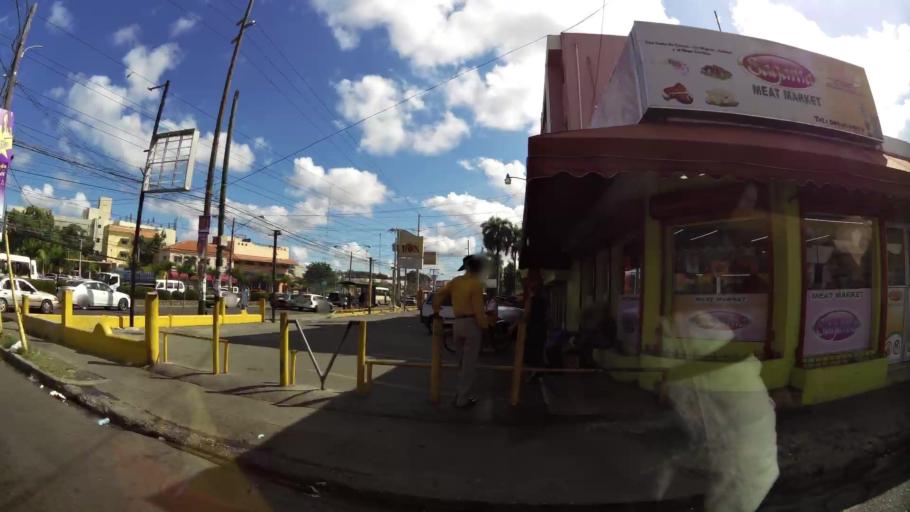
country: DO
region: Santo Domingo
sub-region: Santo Domingo
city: Santo Domingo Este
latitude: 18.5100
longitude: -69.8499
